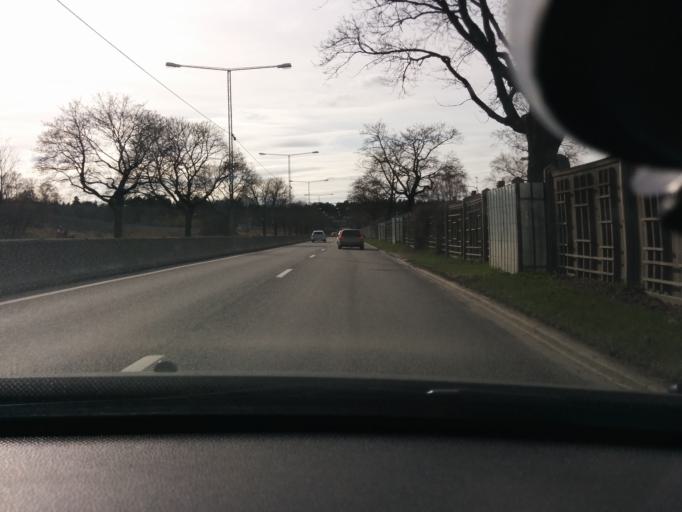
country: SE
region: Stockholm
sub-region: Stockholms Kommun
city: Bromma
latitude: 59.3423
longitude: 17.9152
